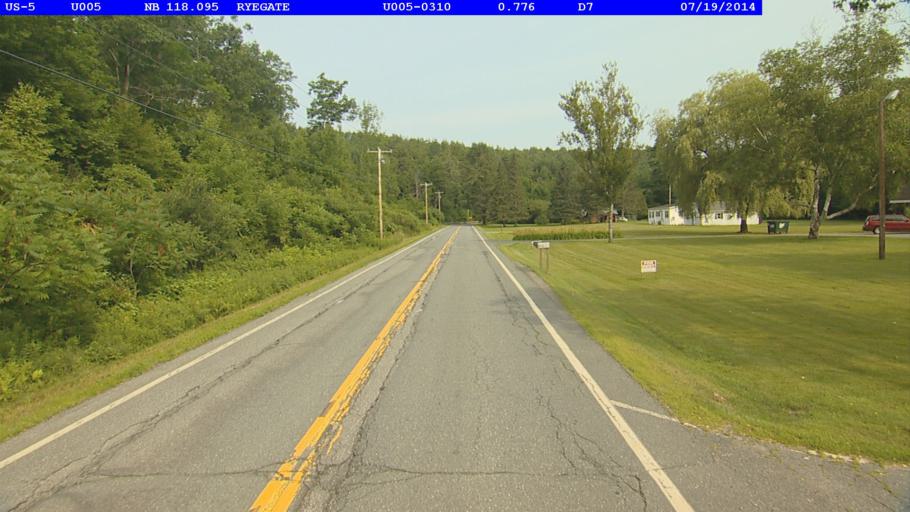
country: US
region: New Hampshire
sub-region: Grafton County
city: Woodsville
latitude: 44.1672
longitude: -72.0549
